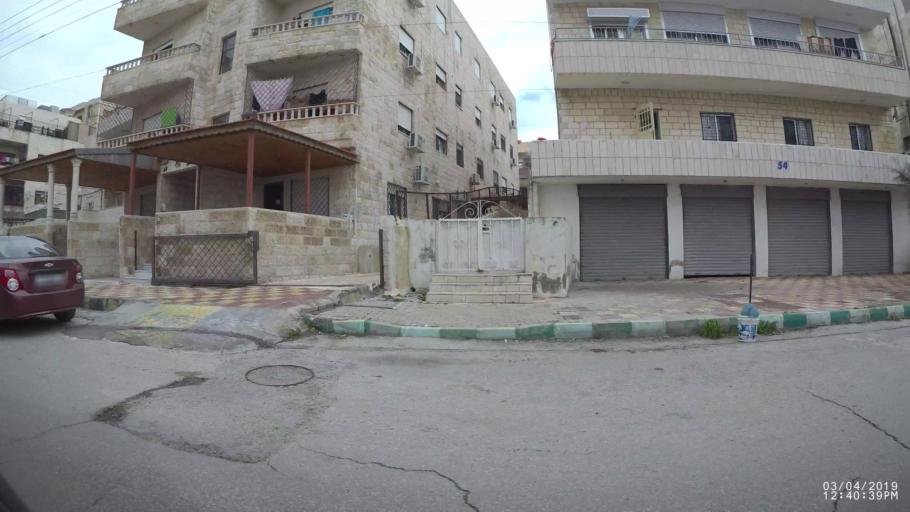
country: JO
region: Amman
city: Wadi as Sir
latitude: 31.9598
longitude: 35.8353
